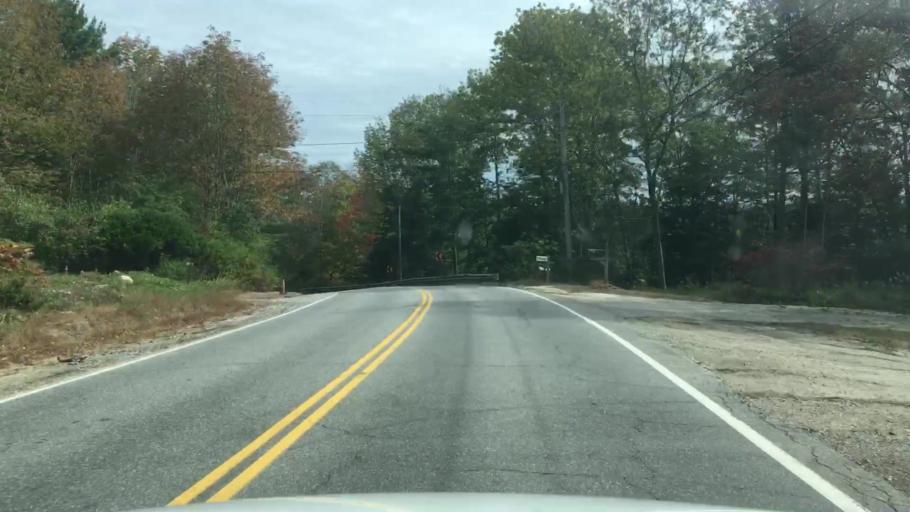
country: US
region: Maine
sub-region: Sagadahoc County
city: Topsham
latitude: 43.9344
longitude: -70.0153
